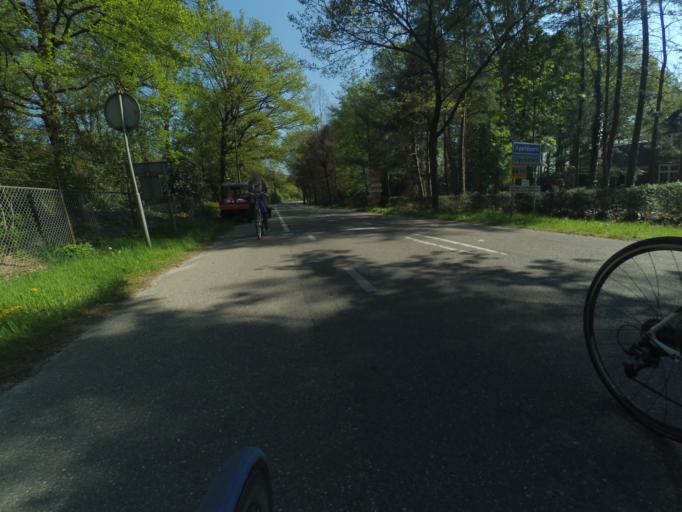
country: NL
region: Gelderland
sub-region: Gemeente Apeldoorn
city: Beekbergen
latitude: 52.1782
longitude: 5.9200
